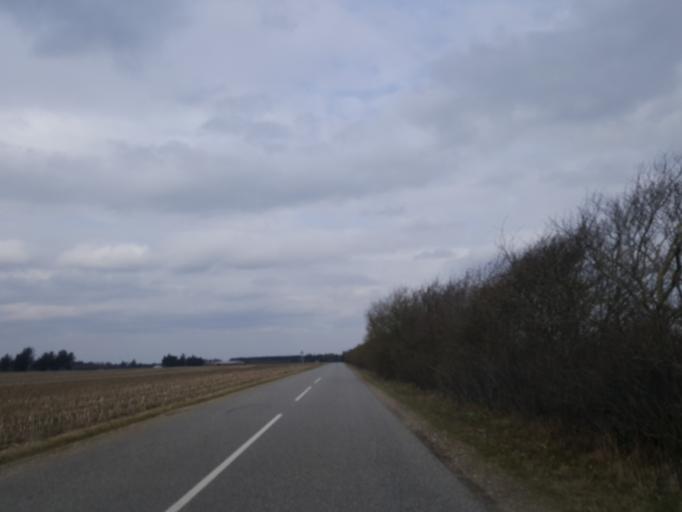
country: DK
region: Central Jutland
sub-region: Holstebro Kommune
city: Ulfborg
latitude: 56.3396
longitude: 8.3068
